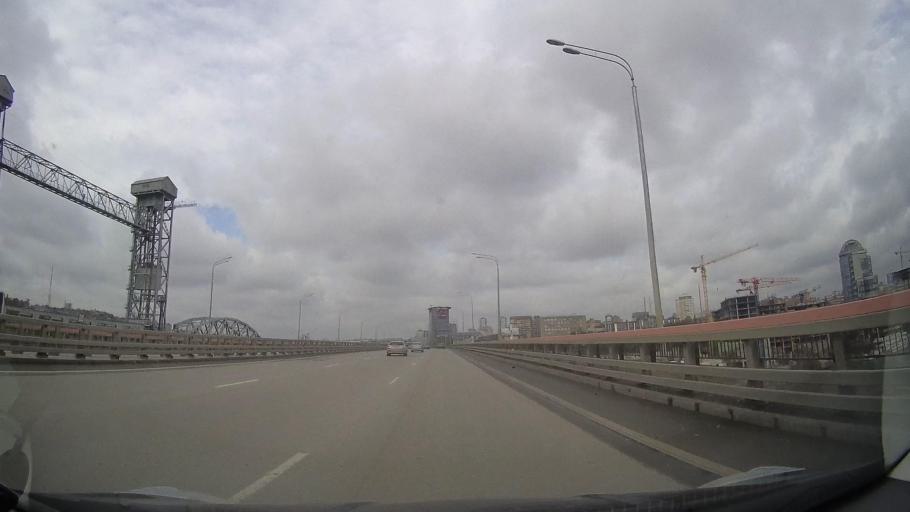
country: RU
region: Rostov
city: Rostov-na-Donu
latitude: 47.2096
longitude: 39.7032
